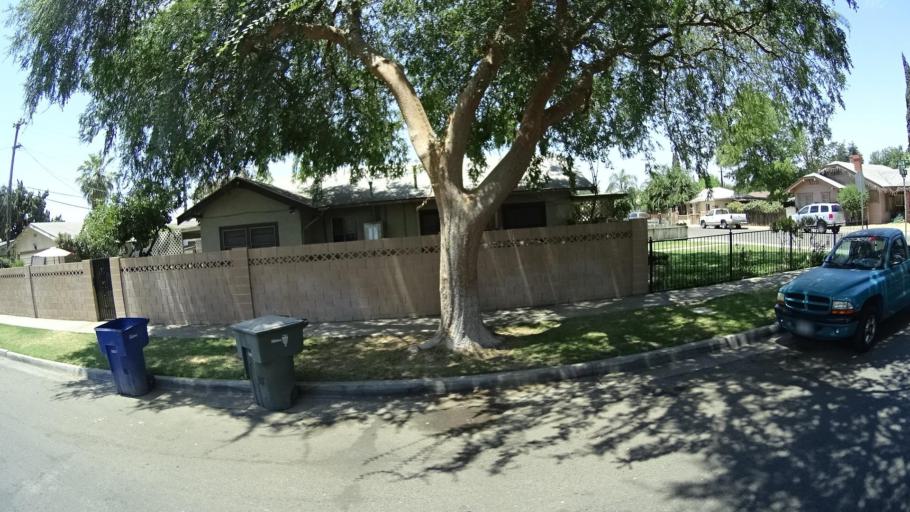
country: US
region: California
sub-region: Fresno County
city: Fresno
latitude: 36.7333
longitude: -119.7617
